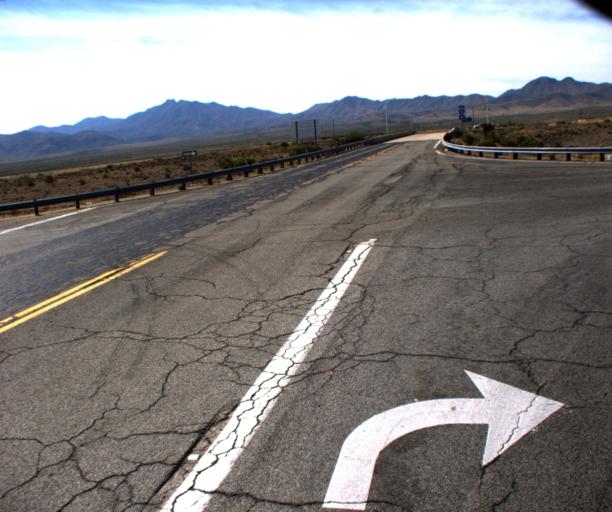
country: US
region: Arizona
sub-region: Cochise County
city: Willcox
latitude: 32.3598
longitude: -109.6816
